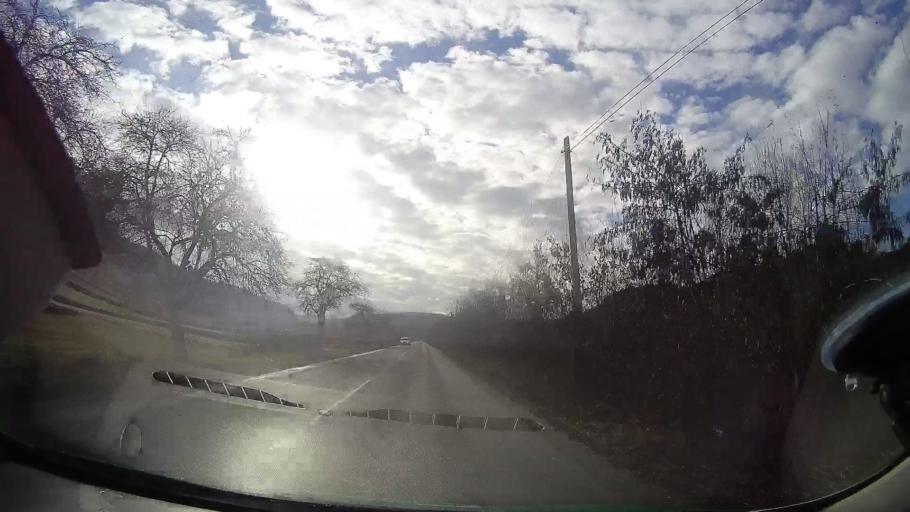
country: RO
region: Cluj
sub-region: Comuna Savadisla
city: Savadisla
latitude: 46.6829
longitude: 23.4561
